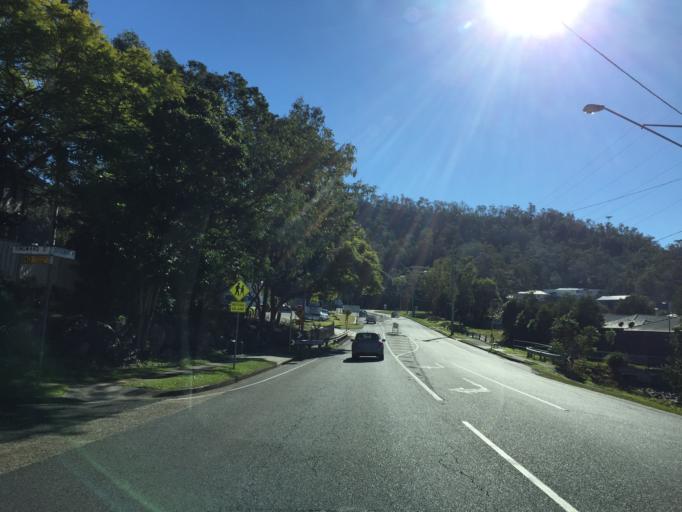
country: AU
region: Queensland
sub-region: Moreton Bay
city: Ferny Hills
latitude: -27.4318
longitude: 152.9429
